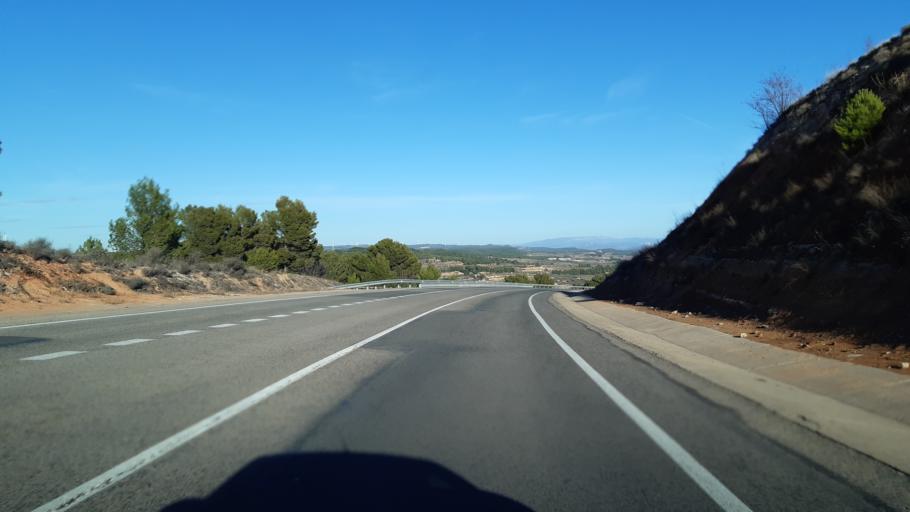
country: ES
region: Catalonia
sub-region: Provincia de Tarragona
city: Bot
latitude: 41.0538
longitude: 0.3918
